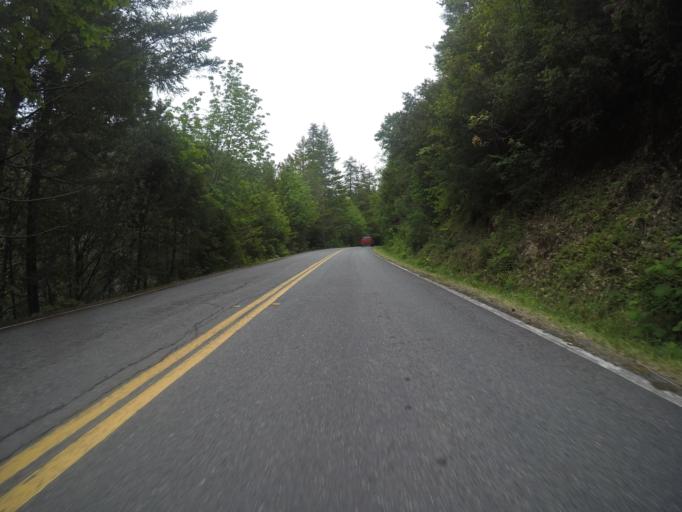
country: US
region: California
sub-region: Del Norte County
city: Bertsch-Oceanview
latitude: 41.7265
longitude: -123.9620
